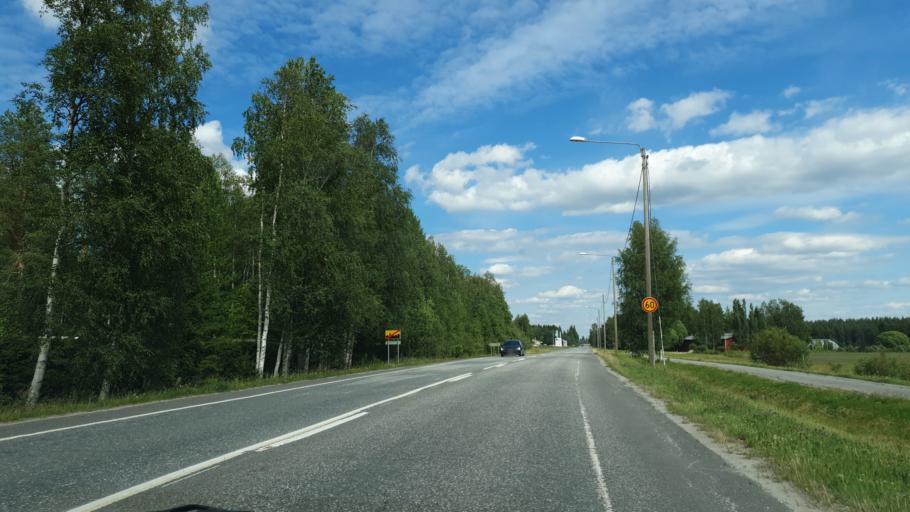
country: FI
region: Kainuu
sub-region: Kajaani
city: Kajaani
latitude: 64.2482
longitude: 27.7693
